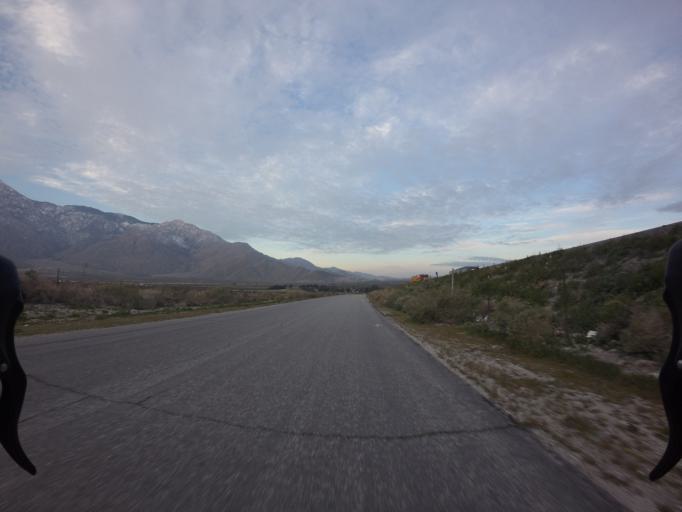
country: US
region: California
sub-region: Riverside County
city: Garnet
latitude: 33.9218
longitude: -116.6533
